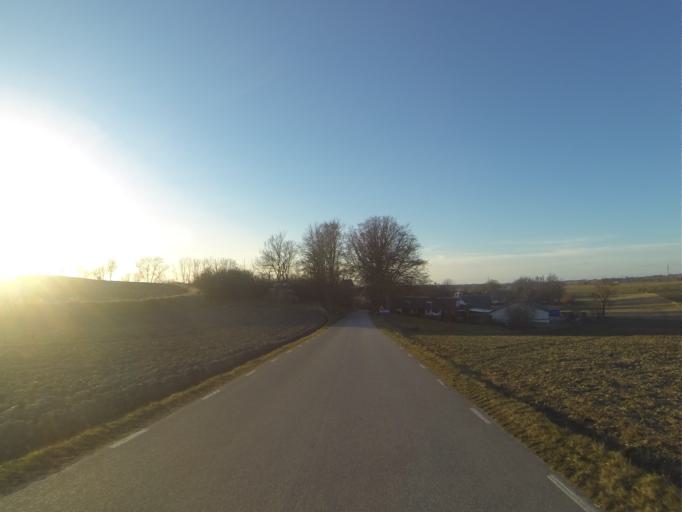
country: SE
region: Skane
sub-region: Staffanstorps Kommun
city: Staffanstorp
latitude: 55.6069
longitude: 13.1803
